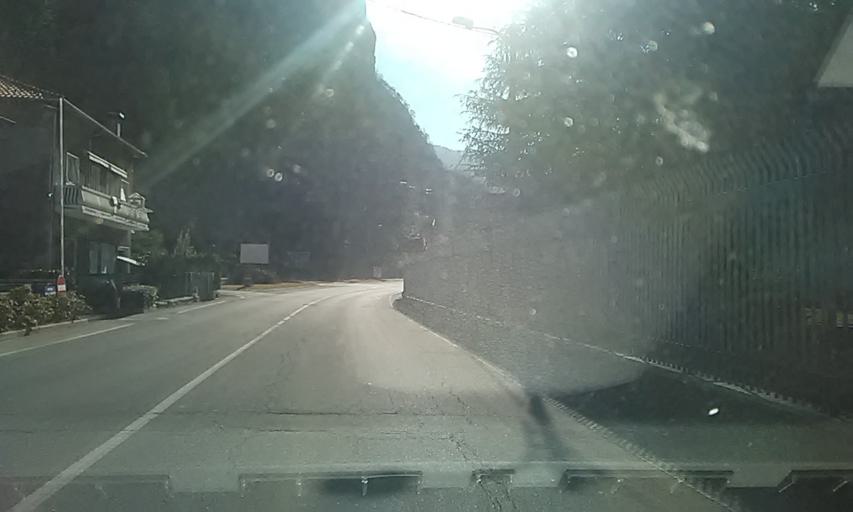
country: IT
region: Piedmont
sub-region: Provincia di Vercelli
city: Varallo
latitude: 45.8097
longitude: 8.2695
